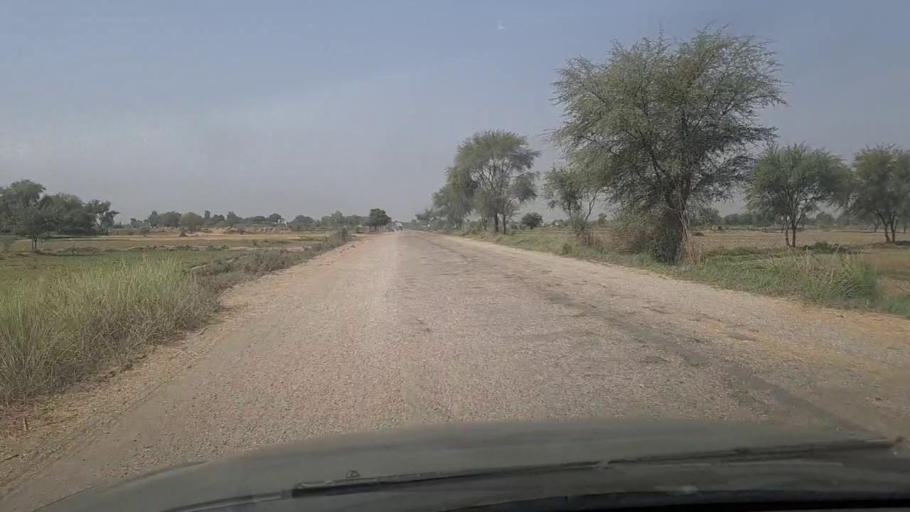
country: PK
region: Sindh
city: Khanpur
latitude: 27.9007
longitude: 69.4972
